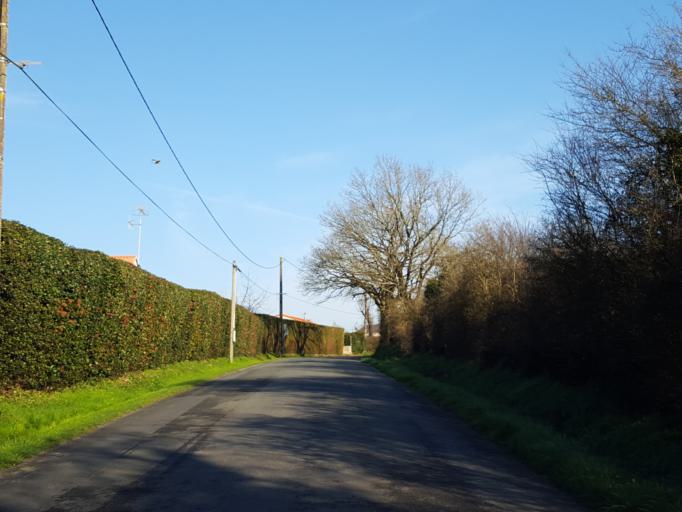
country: FR
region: Pays de la Loire
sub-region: Departement de la Vendee
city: La Chaize-le-Vicomte
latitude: 46.6744
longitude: -1.2840
